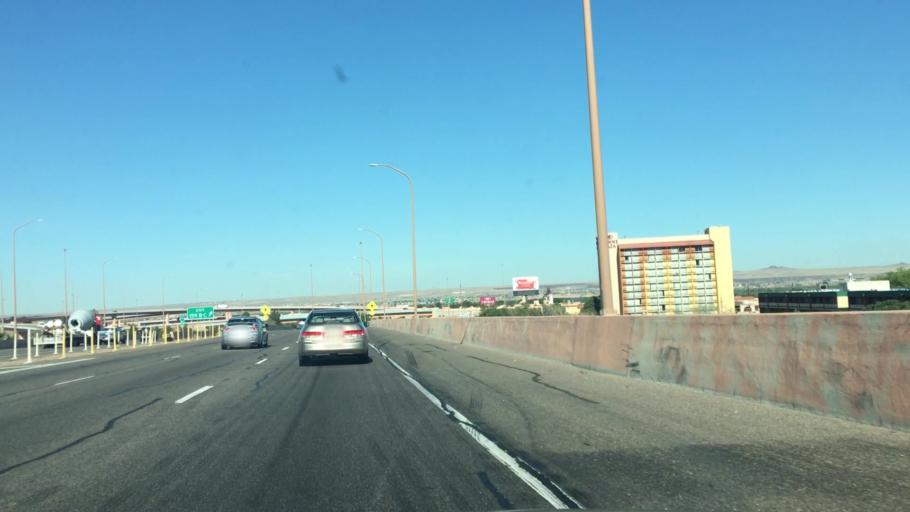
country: US
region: New Mexico
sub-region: Bernalillo County
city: Albuquerque
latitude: 35.1072
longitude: -106.6210
